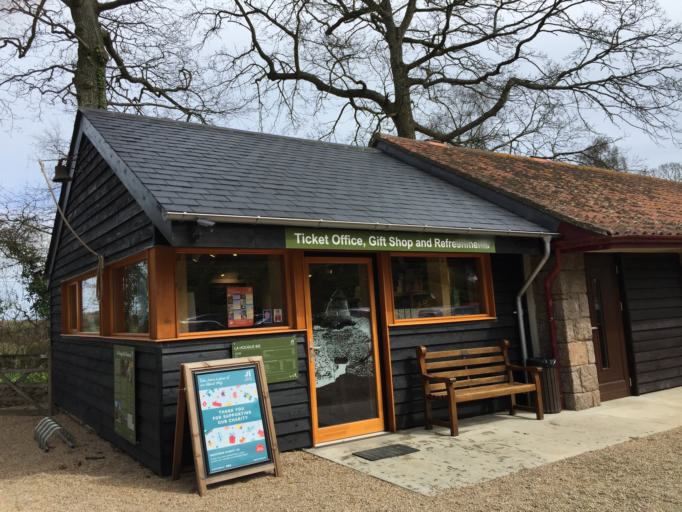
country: JE
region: St Helier
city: Saint Helier
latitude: 49.2008
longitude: -2.0640
